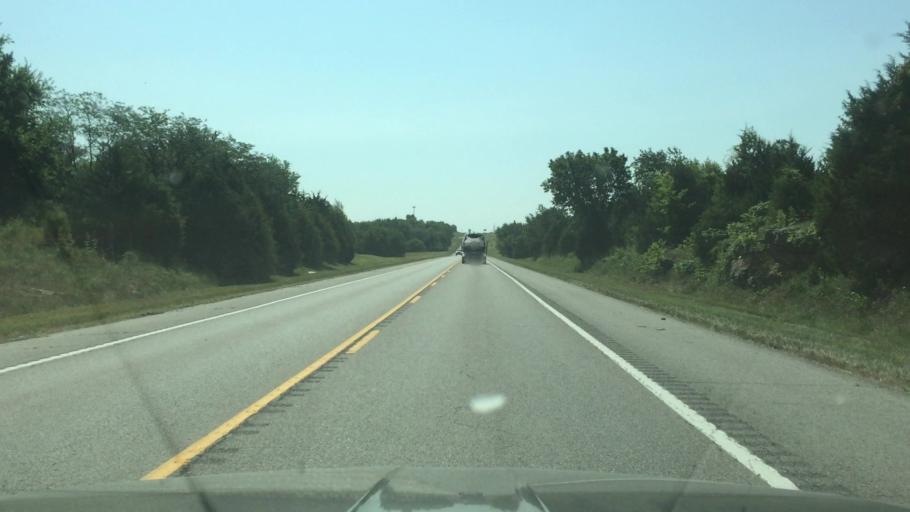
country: US
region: Missouri
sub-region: Pettis County
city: Sedalia
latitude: 38.6902
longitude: -93.0494
